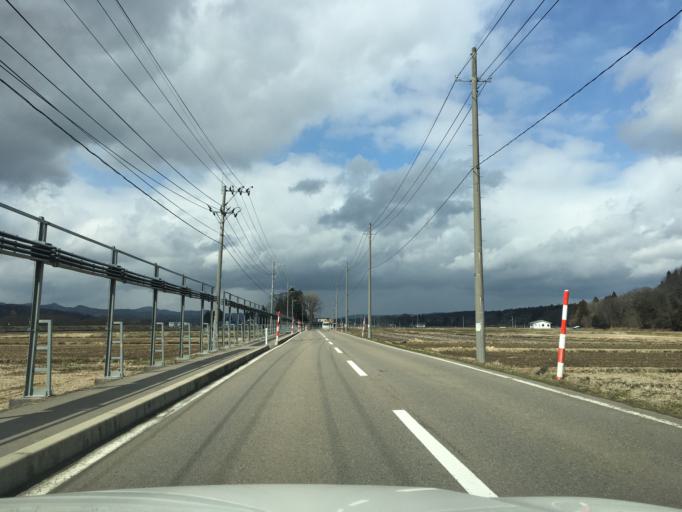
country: JP
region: Akita
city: Takanosu
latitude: 40.1318
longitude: 140.3587
